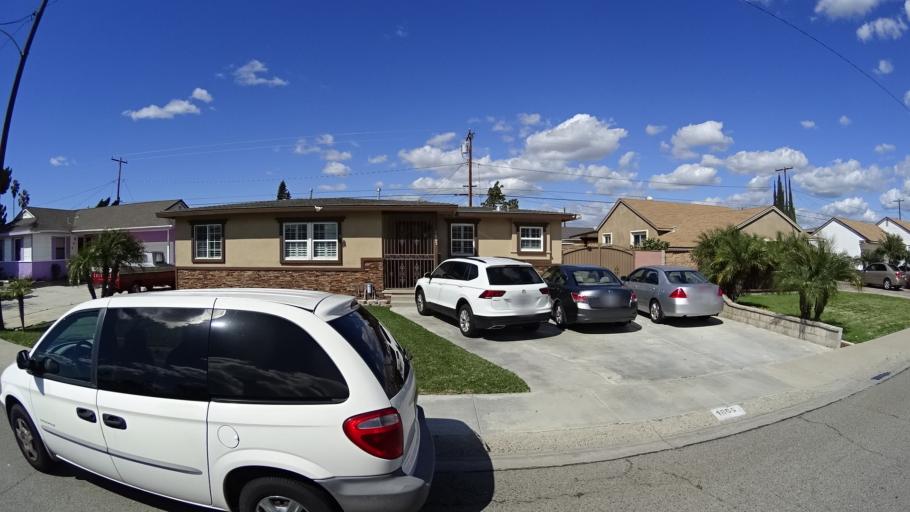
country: US
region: California
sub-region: Orange County
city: Anaheim
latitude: 33.8366
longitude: -117.8921
